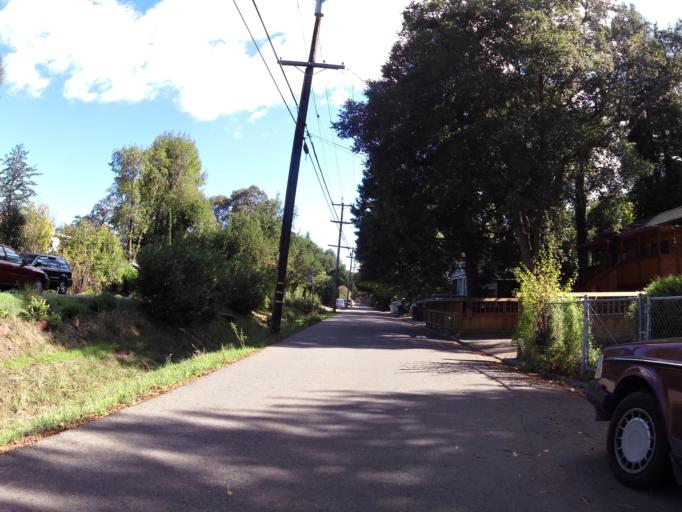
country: US
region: California
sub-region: Marin County
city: Fairfax
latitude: 37.9836
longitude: -122.5796
